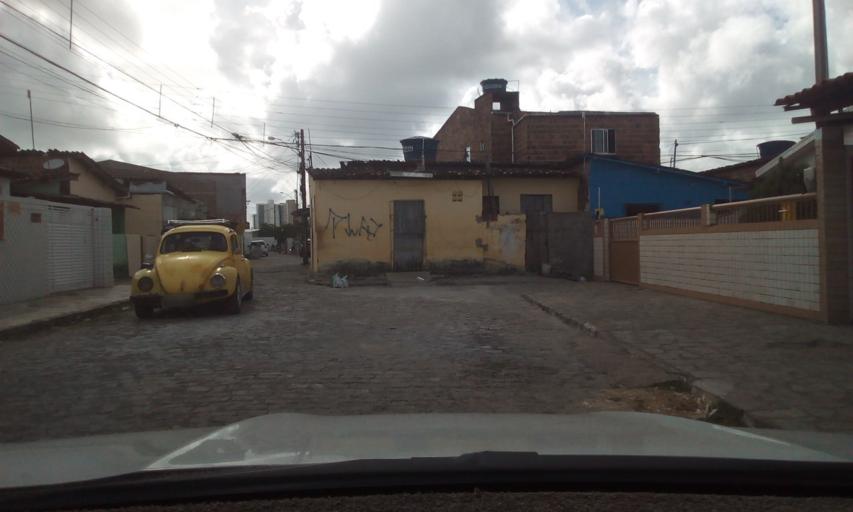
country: BR
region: Paraiba
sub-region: Joao Pessoa
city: Joao Pessoa
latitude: -7.1119
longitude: -34.8664
